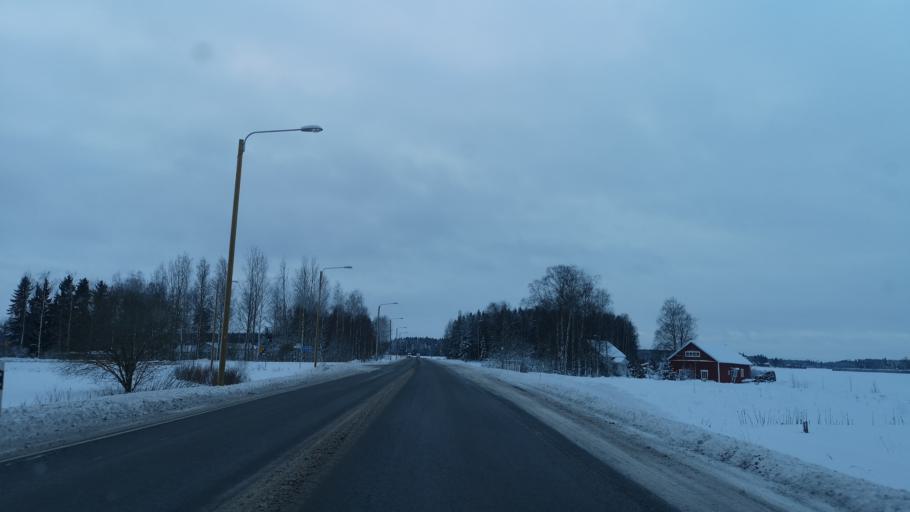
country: FI
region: Varsinais-Suomi
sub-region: Loimaa
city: Loimaa
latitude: 60.8854
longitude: 23.0900
